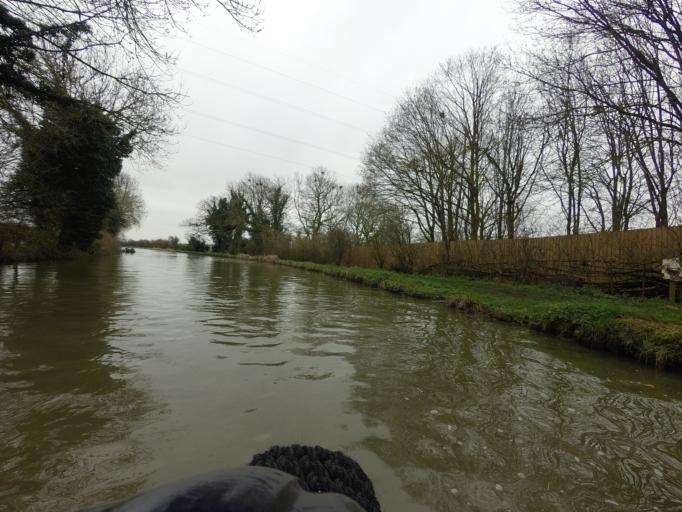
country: GB
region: England
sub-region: Central Bedfordshire
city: Leighton Buzzard
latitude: 51.8892
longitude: -0.6628
